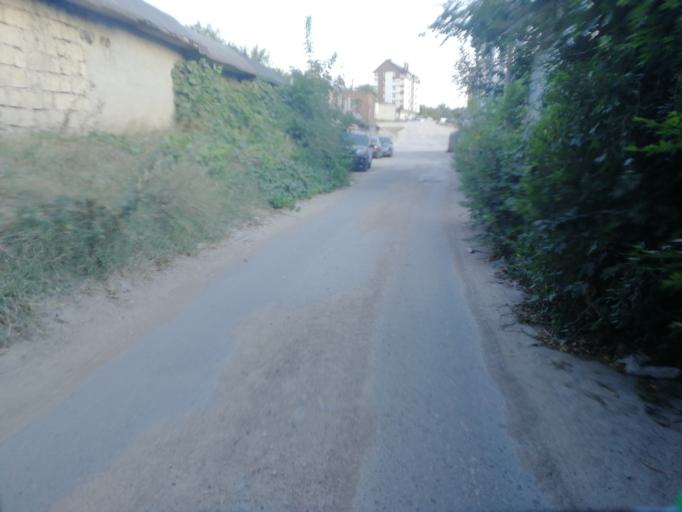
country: MD
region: Chisinau
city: Chisinau
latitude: 47.0287
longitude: 28.8698
